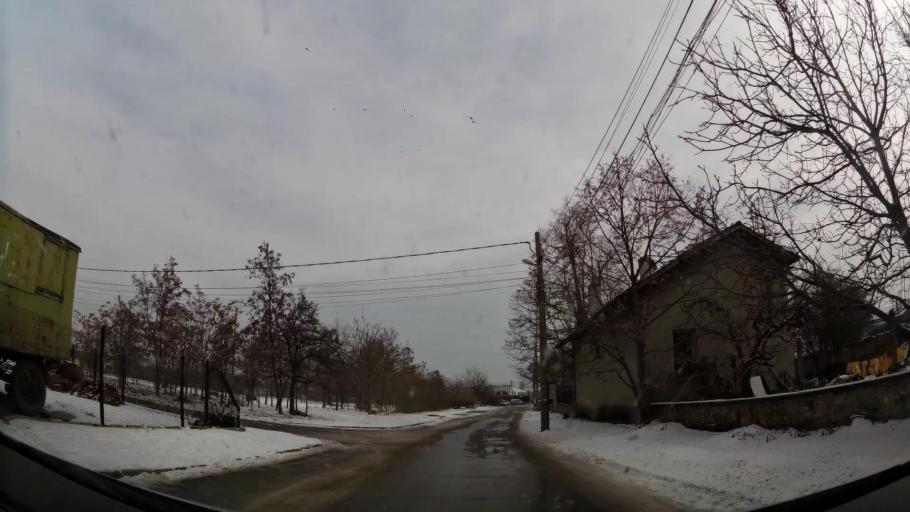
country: BG
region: Sofia-Capital
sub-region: Stolichna Obshtina
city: Sofia
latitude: 42.7109
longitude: 23.4065
